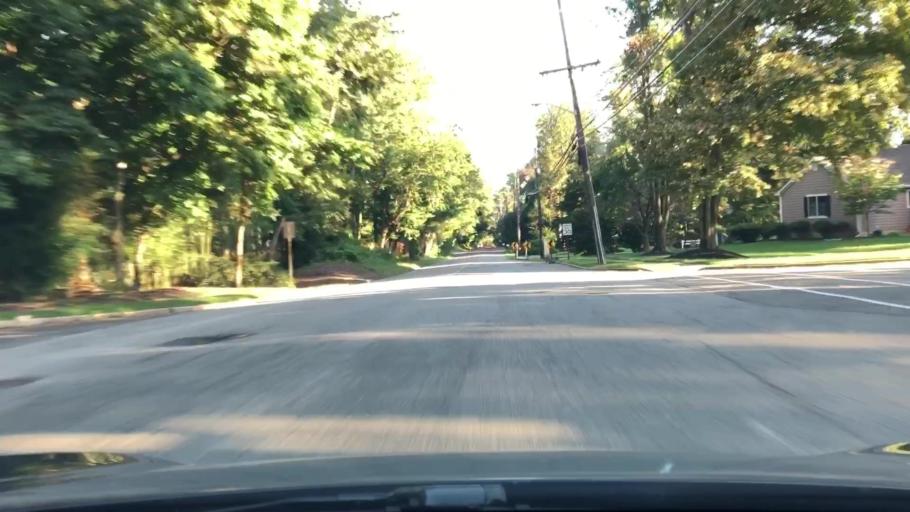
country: US
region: New Jersey
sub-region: Mercer County
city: Lawrenceville
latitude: 40.3055
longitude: -74.7295
